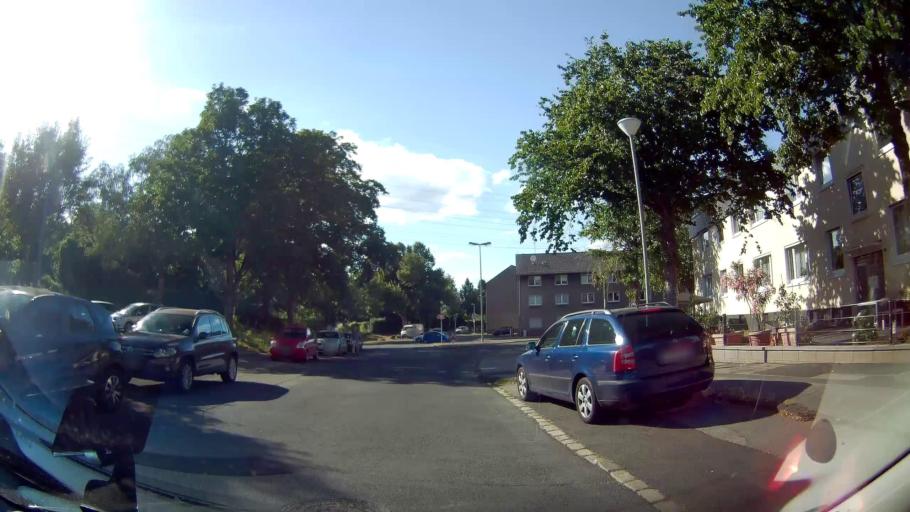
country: DE
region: North Rhine-Westphalia
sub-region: Regierungsbezirk Dusseldorf
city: Essen
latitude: 51.4726
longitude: 6.9971
